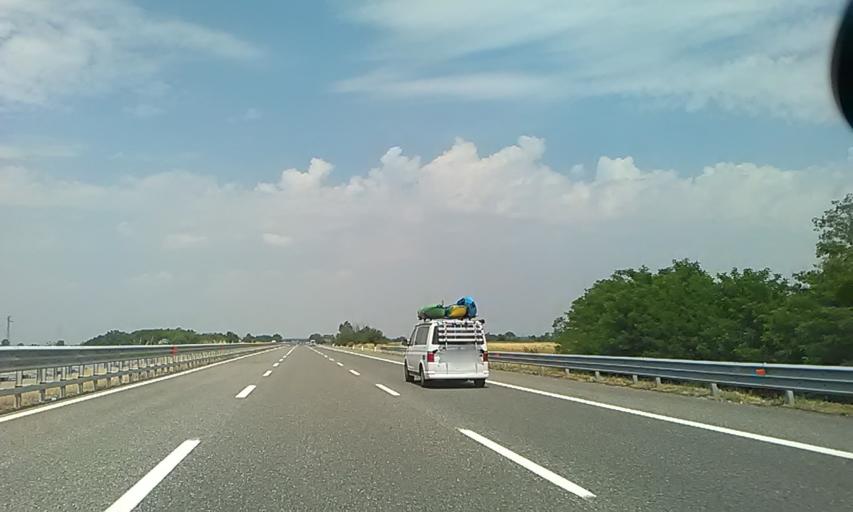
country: IT
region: Piedmont
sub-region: Provincia di Alessandria
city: Castelspina
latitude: 44.7959
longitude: 8.6100
